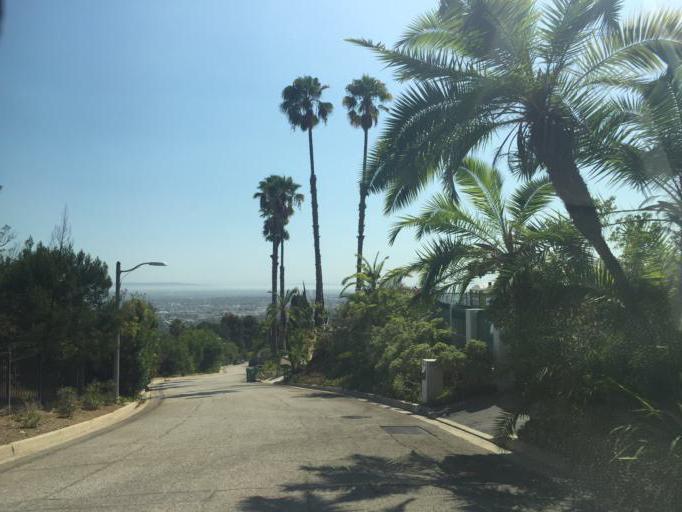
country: US
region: California
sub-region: Los Angeles County
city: Beverly Hills
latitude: 34.0980
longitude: -118.3973
